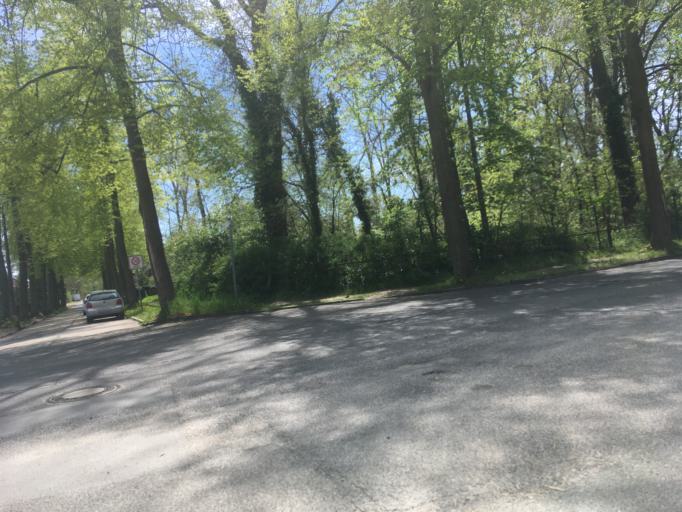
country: DE
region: Brandenburg
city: Zeuthen
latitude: 52.3441
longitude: 13.6089
